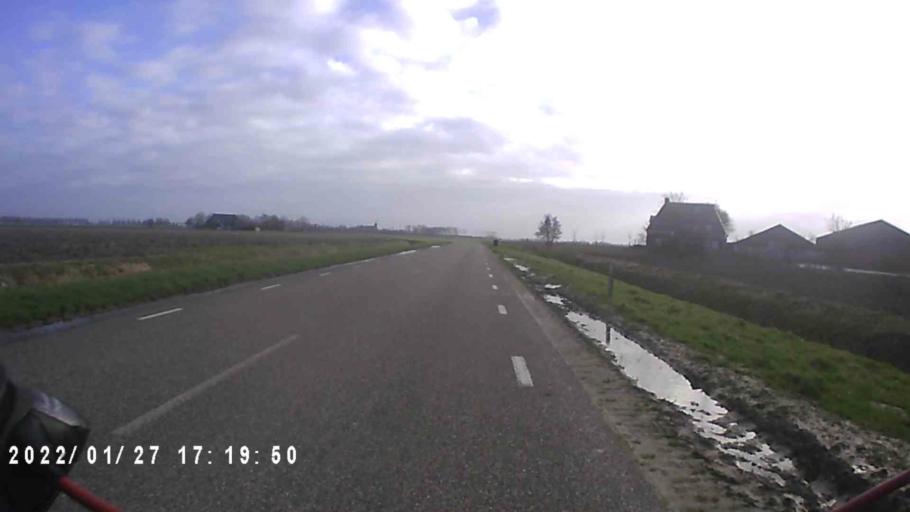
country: NL
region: Friesland
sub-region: Gemeente Dongeradeel
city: Anjum
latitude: 53.3852
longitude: 6.1121
